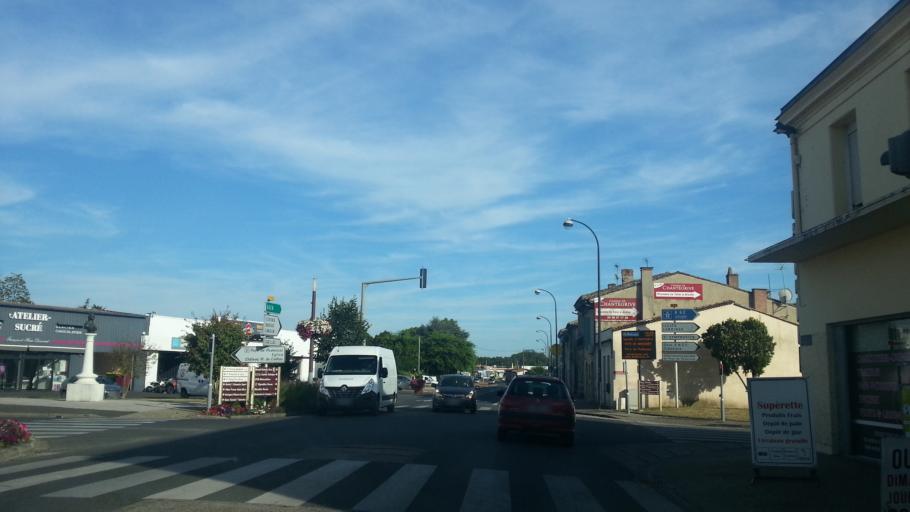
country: FR
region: Aquitaine
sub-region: Departement de la Gironde
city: Podensac
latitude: 44.6498
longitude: -0.3544
